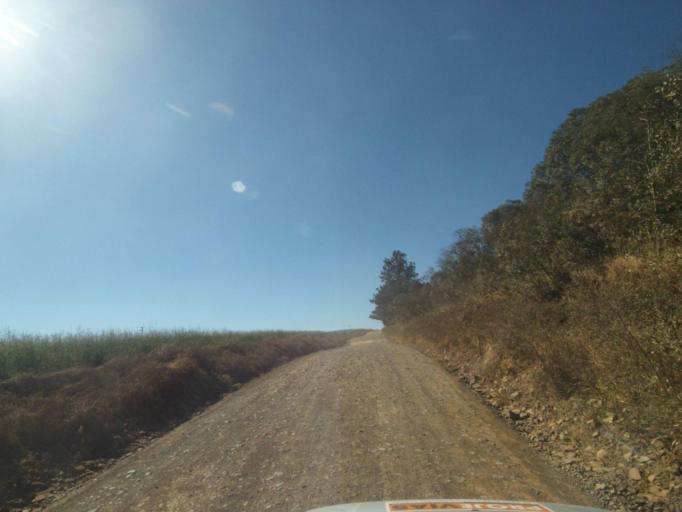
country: BR
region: Parana
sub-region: Reserva
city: Reserva
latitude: -24.6268
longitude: -50.6205
